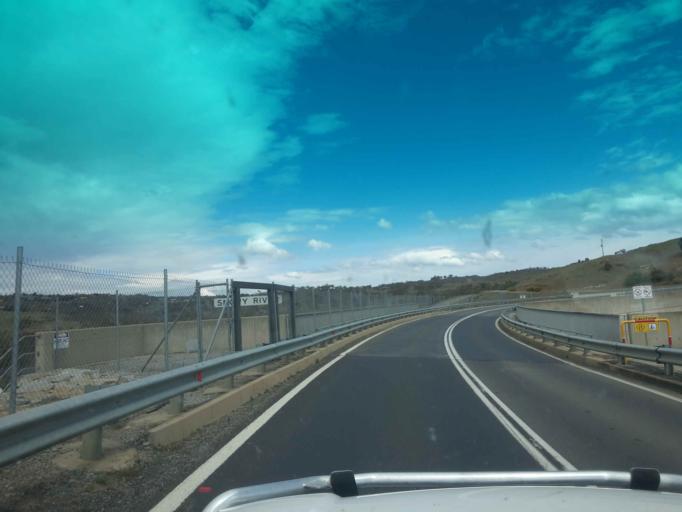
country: AU
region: New South Wales
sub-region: Snowy River
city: Jindabyne
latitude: -36.4344
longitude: 148.6330
